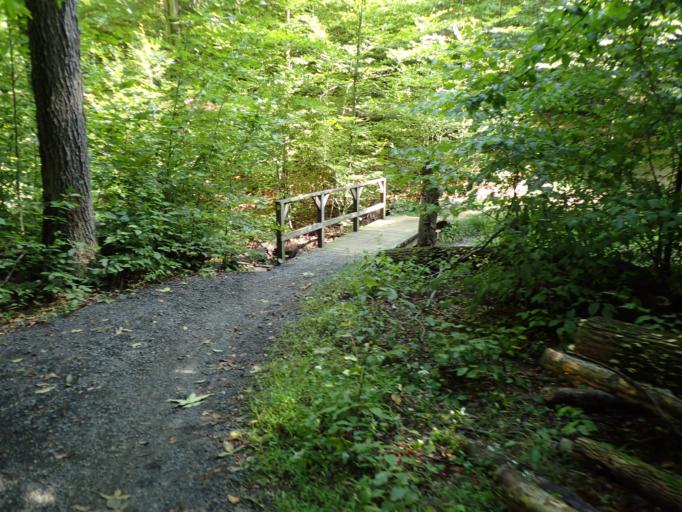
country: US
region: New Jersey
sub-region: Morris County
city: Mendham
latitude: 40.7839
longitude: -74.5493
